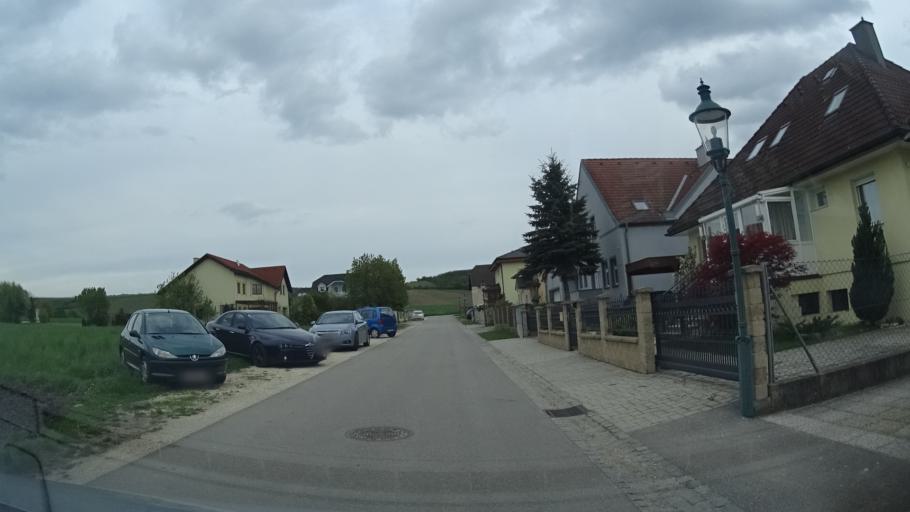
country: AT
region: Lower Austria
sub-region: Politischer Bezirk Korneuburg
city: Stetten
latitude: 48.3657
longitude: 16.3865
